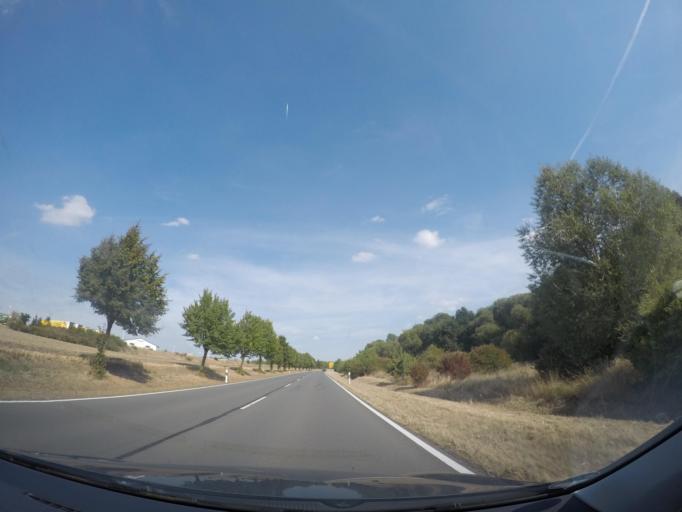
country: DE
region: Saxony-Anhalt
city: Heudeber
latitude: 51.9703
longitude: 10.8411
